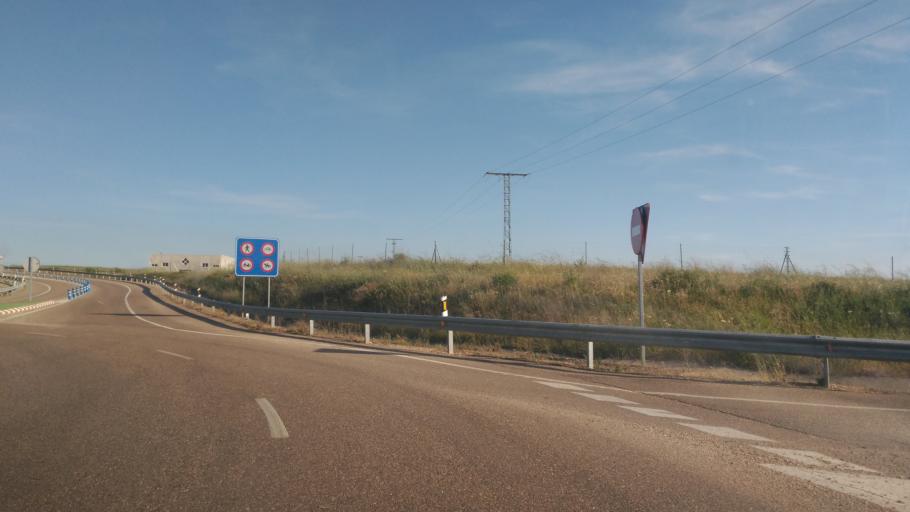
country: ES
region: Castille and Leon
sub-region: Provincia de Zamora
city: Cazurra
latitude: 41.4168
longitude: -5.7240
